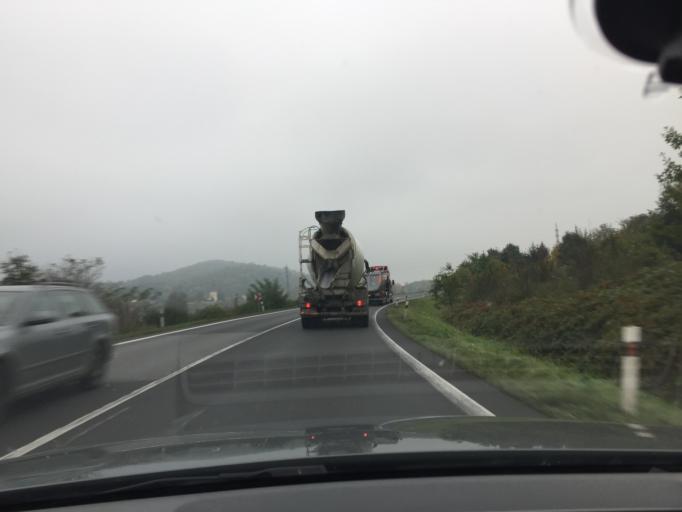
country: CZ
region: Ustecky
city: Lovosice
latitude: 50.5428
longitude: 14.0529
